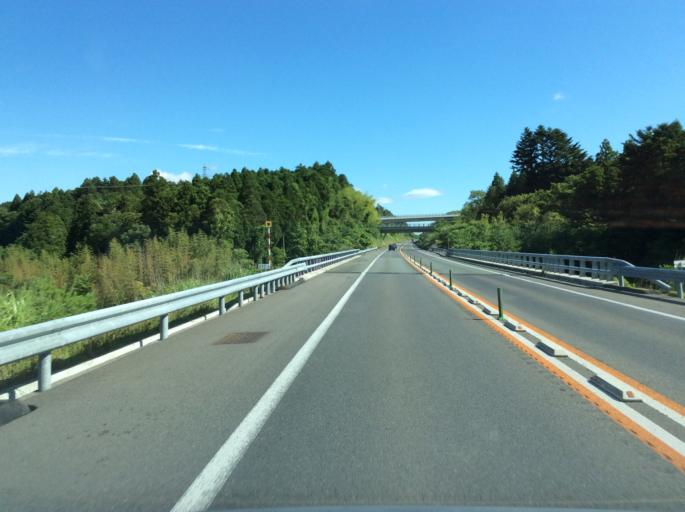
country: JP
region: Fukushima
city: Namie
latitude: 37.3240
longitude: 140.9907
